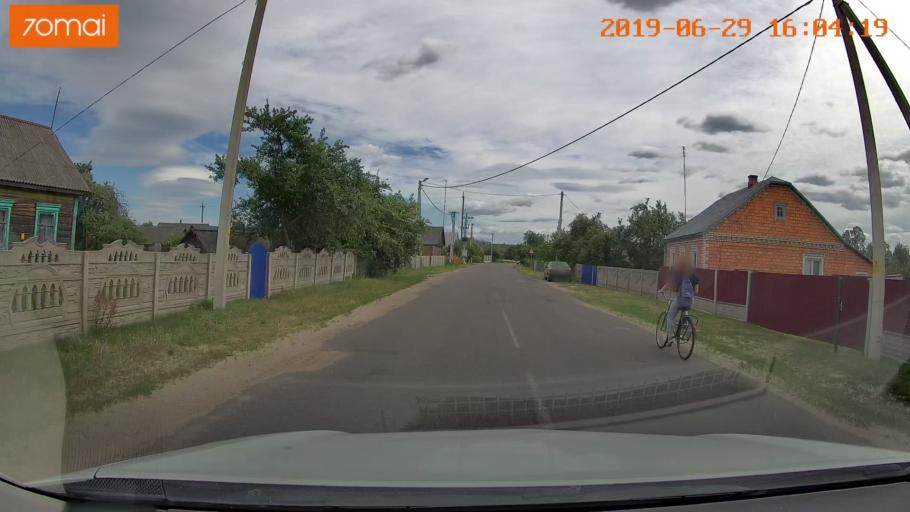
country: BY
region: Brest
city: Luninyets
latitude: 52.2236
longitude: 27.0243
